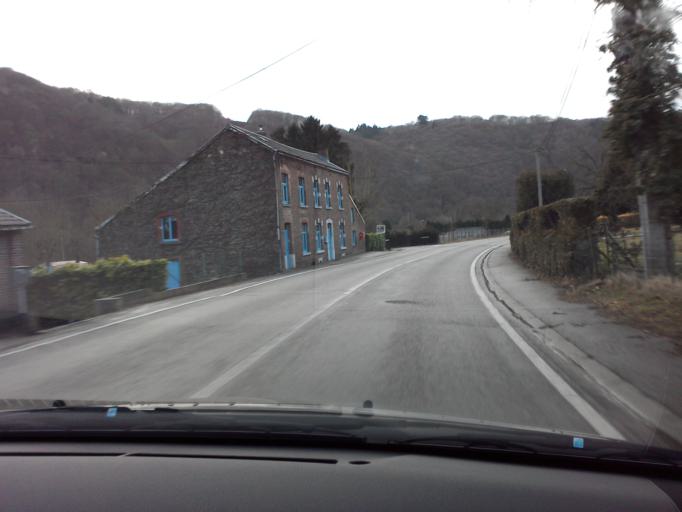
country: BE
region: Wallonia
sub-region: Province de Liege
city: Aywaille
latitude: 50.4576
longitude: 5.7193
